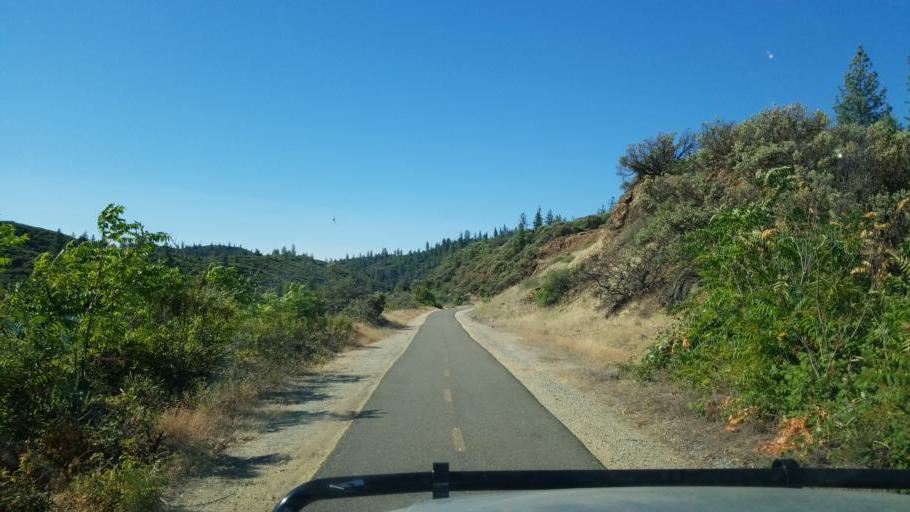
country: US
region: California
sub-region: Shasta County
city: Shasta
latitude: 40.6711
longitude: -122.4613
